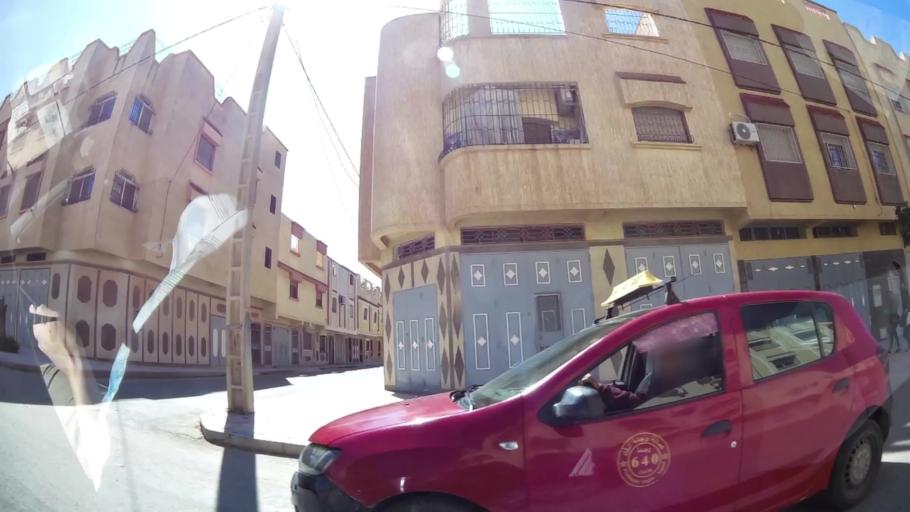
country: MA
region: Oriental
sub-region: Oujda-Angad
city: Oujda
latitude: 34.6847
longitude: -1.9382
